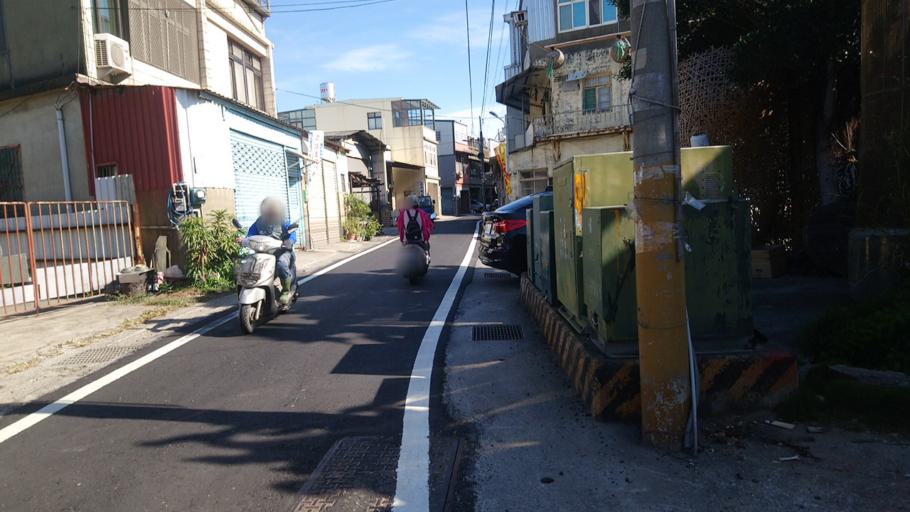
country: TW
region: Taiwan
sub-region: Miaoli
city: Miaoli
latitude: 24.6766
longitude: 120.8874
